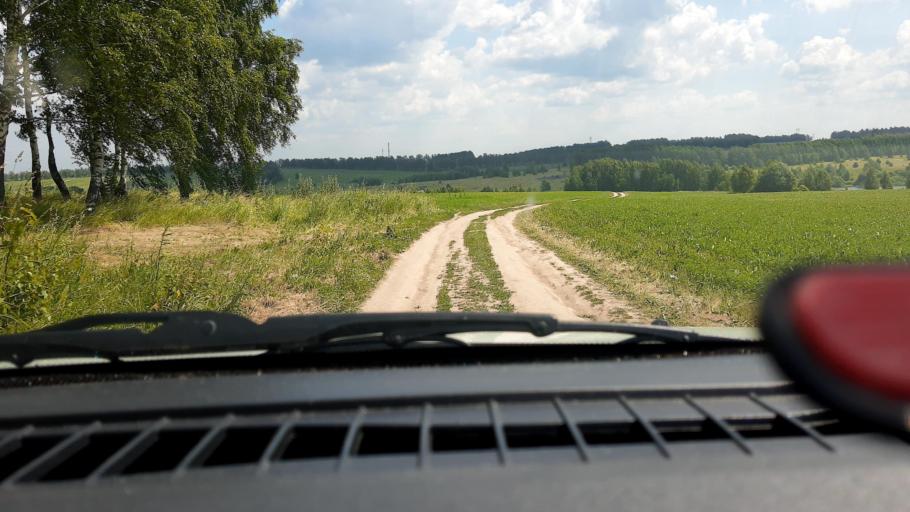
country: RU
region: Nizjnij Novgorod
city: Afonino
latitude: 56.1188
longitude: 44.0351
